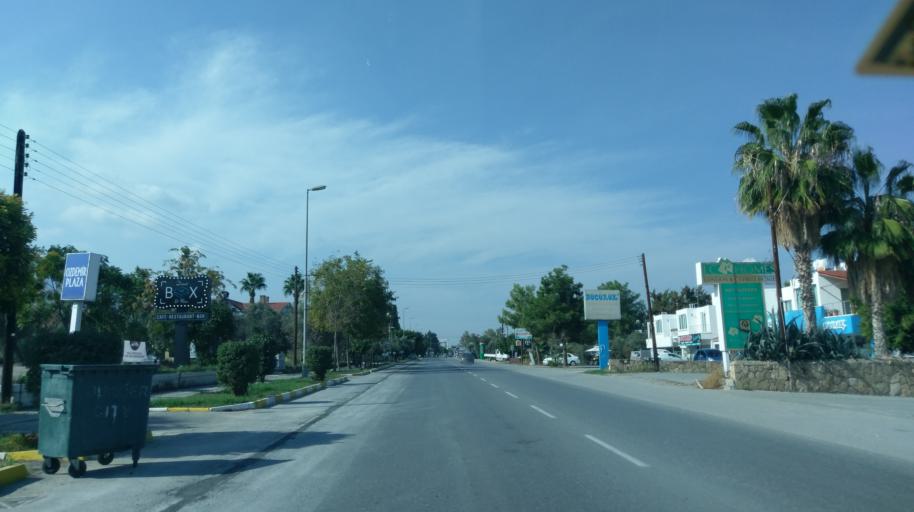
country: CY
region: Keryneia
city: Kyrenia
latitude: 35.3399
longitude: 33.2952
